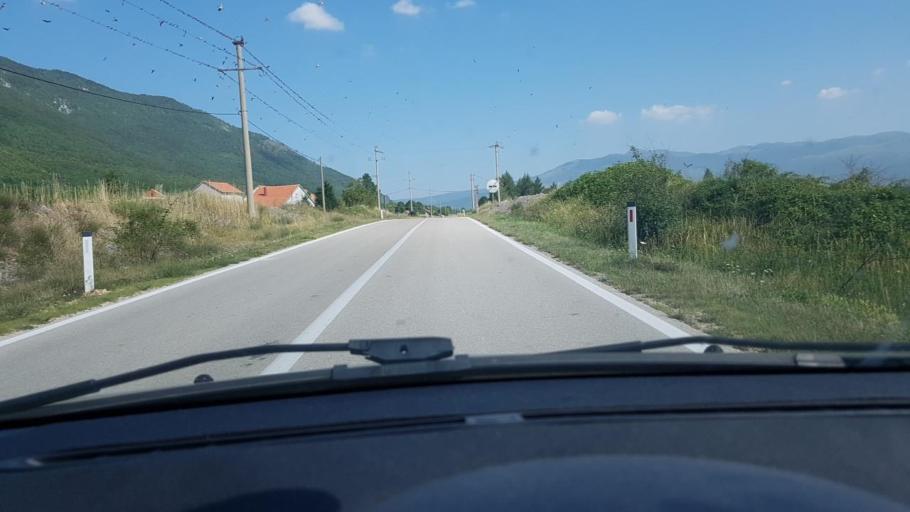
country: BA
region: Federation of Bosnia and Herzegovina
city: Glamoc
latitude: 44.0222
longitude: 16.5992
